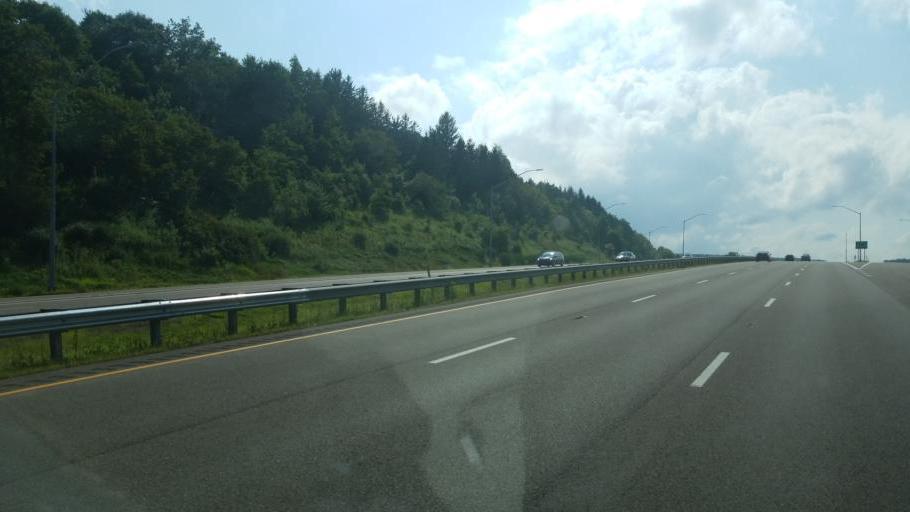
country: US
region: Pennsylvania
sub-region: Somerset County
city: Meyersdale
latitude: 39.6830
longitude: -79.0673
